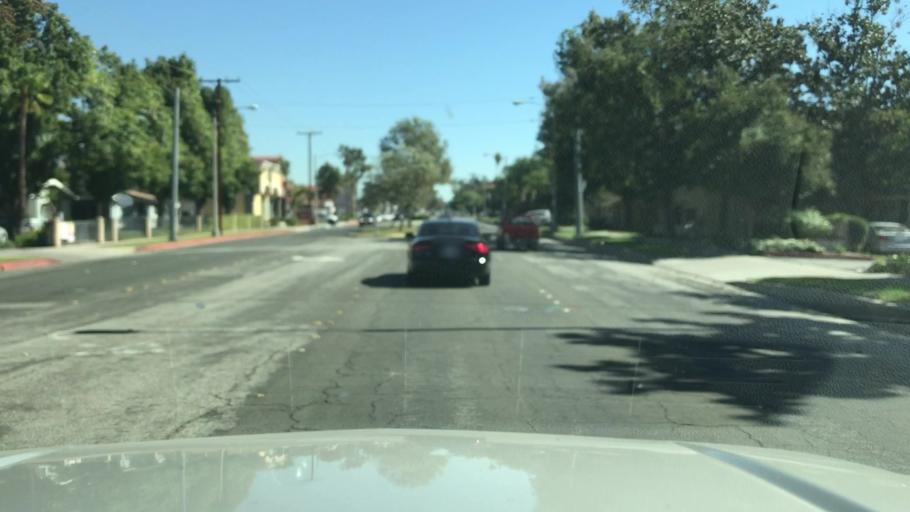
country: US
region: California
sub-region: Los Angeles County
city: Citrus
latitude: 34.1287
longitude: -117.8846
